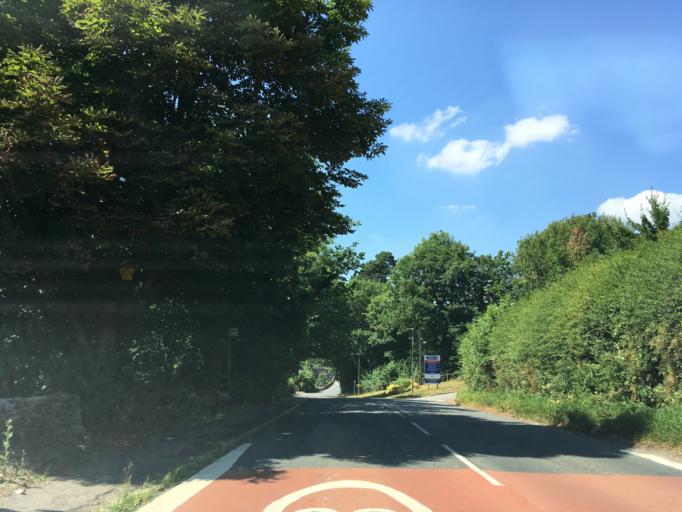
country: GB
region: England
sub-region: Gloucestershire
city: Tetbury
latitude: 51.6344
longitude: -2.1533
